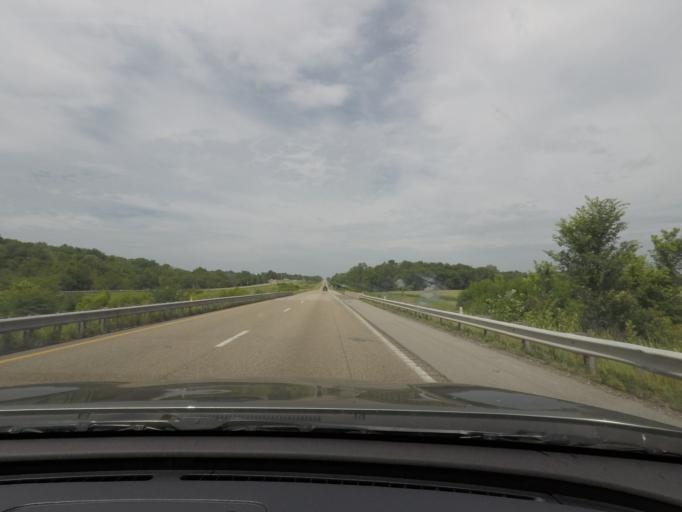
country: US
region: Missouri
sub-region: Montgomery County
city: Montgomery City
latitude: 38.8994
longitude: -91.5898
